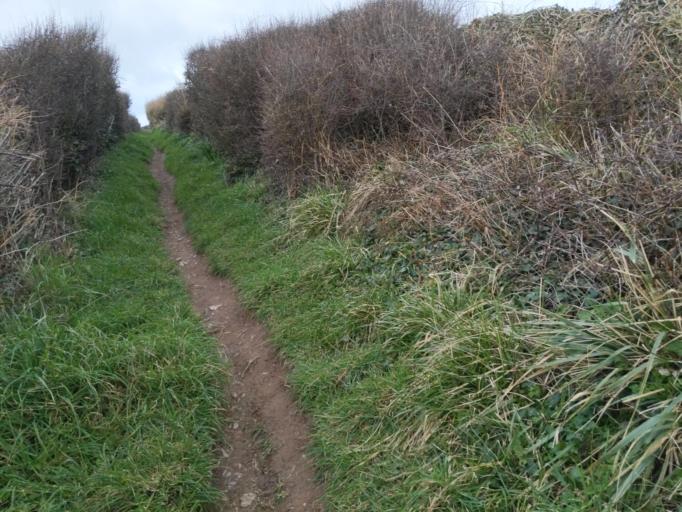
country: GB
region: England
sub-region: Devon
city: Salcombe
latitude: 50.2110
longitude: -3.7297
